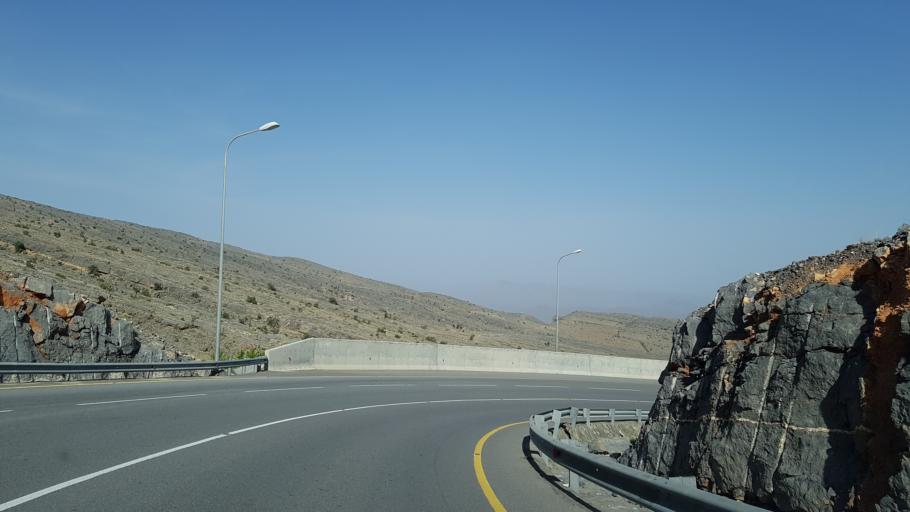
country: OM
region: Muhafazat ad Dakhiliyah
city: Izki
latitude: 23.0053
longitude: 57.6997
